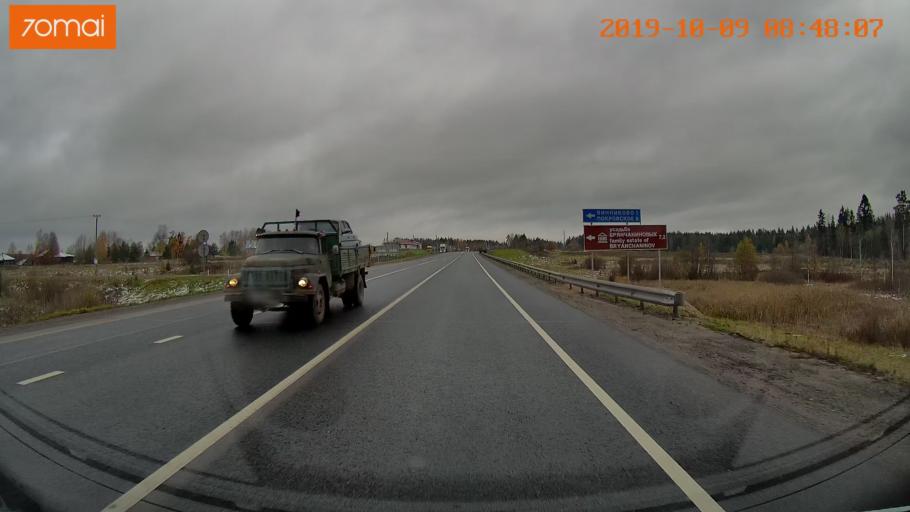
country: RU
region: Vologda
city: Vologda
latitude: 59.0710
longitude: 40.0312
